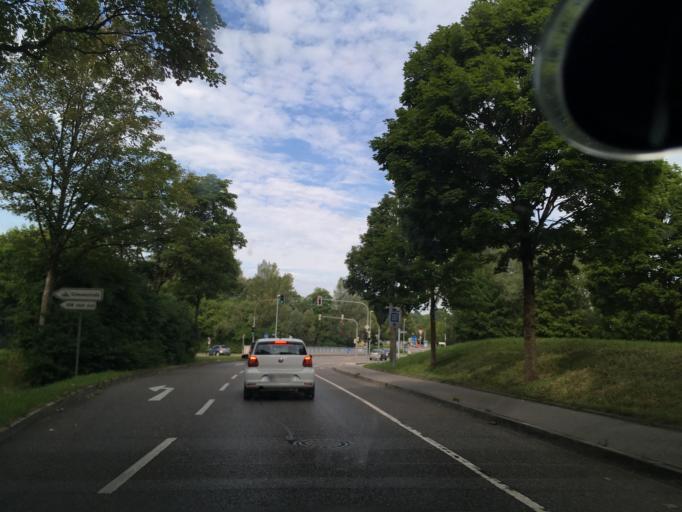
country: DE
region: Baden-Wuerttemberg
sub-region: Tuebingen Region
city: Ravensburg
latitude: 47.7827
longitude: 9.6033
